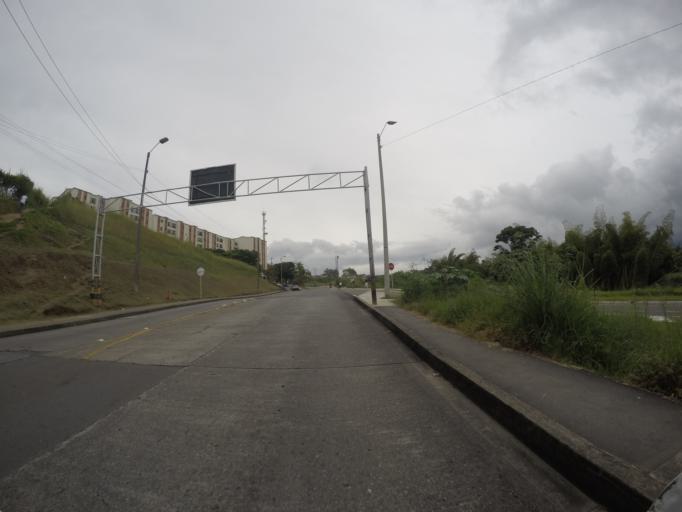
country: CO
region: Risaralda
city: Pereira
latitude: 4.8105
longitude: -75.7331
